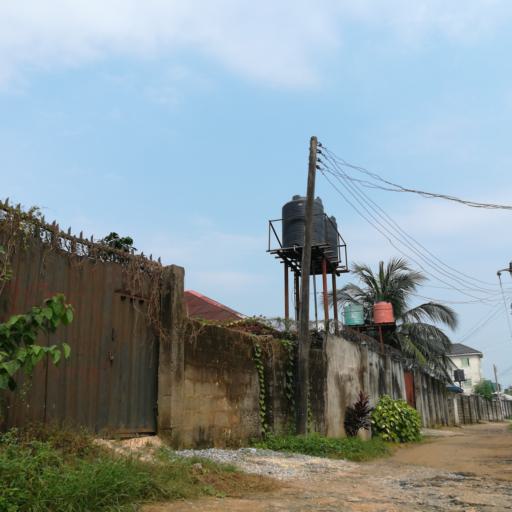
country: NG
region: Rivers
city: Port Harcourt
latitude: 4.8391
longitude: 7.0635
